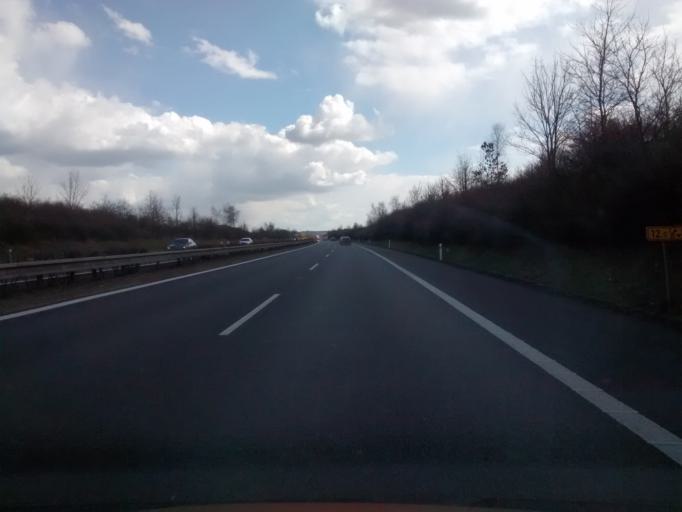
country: CZ
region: Central Bohemia
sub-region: Okres Melnik
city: Veltrusy
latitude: 50.2699
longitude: 14.3602
